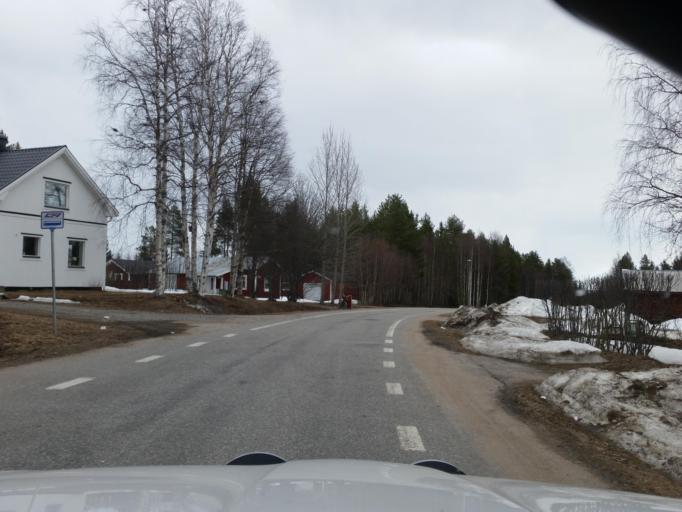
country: SE
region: Norrbotten
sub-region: Pitea Kommun
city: Roknas
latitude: 65.3459
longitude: 21.1494
